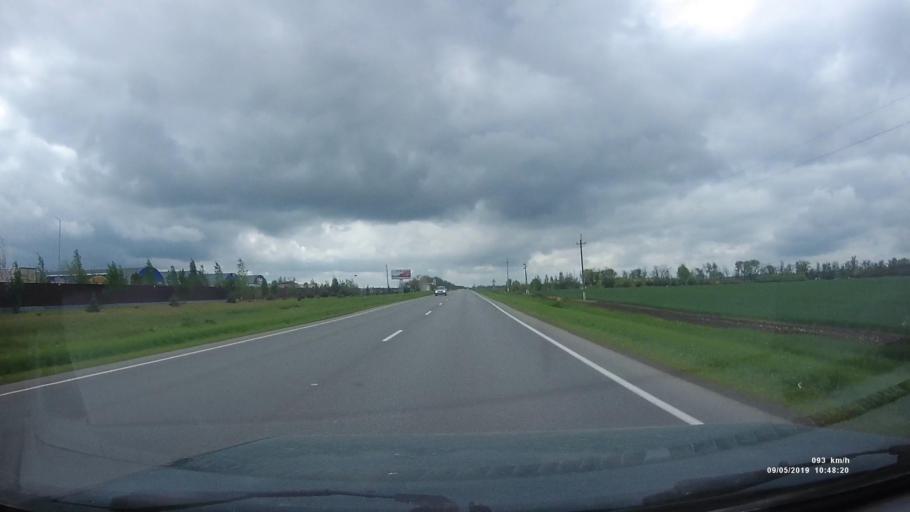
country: RU
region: Rostov
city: Peshkovo
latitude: 46.9580
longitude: 39.3559
